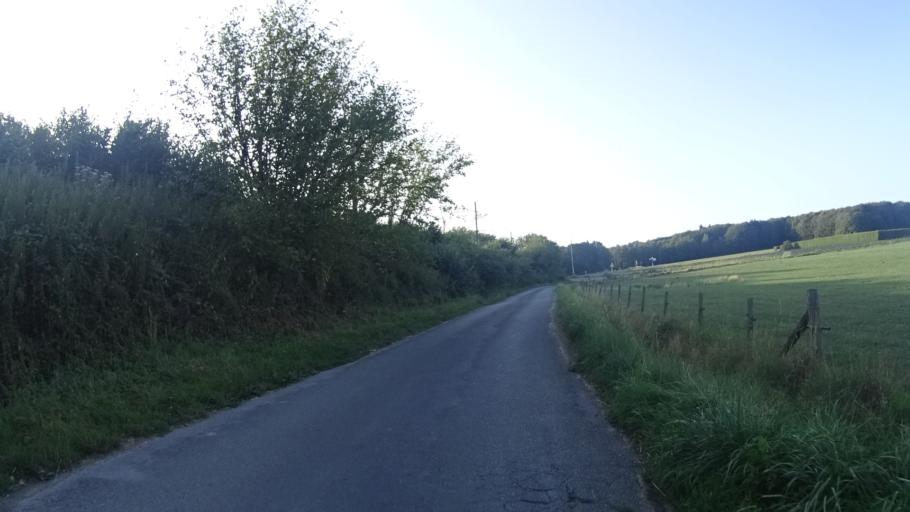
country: BE
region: Flanders
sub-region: Provincie West-Vlaanderen
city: Ieper
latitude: 50.8129
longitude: 2.9401
